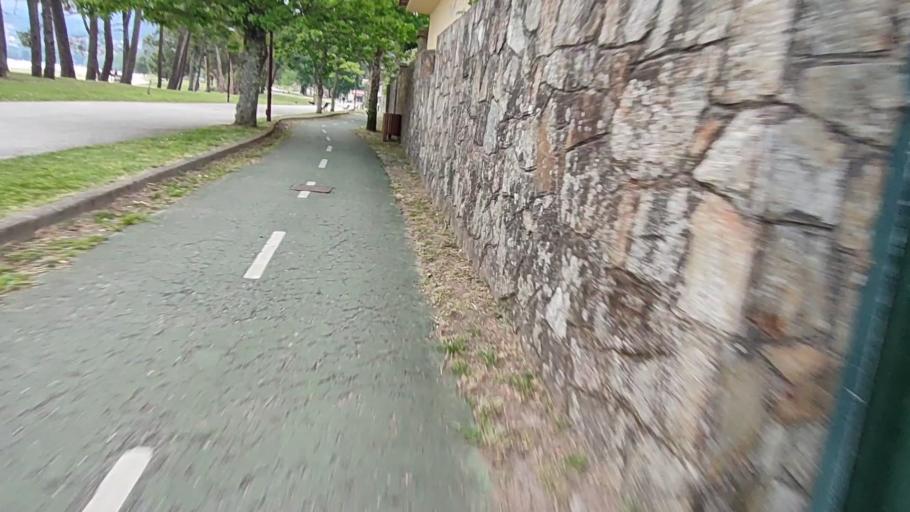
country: ES
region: Galicia
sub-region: Provincia da Coruna
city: Boiro
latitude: 42.6383
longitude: -8.8798
